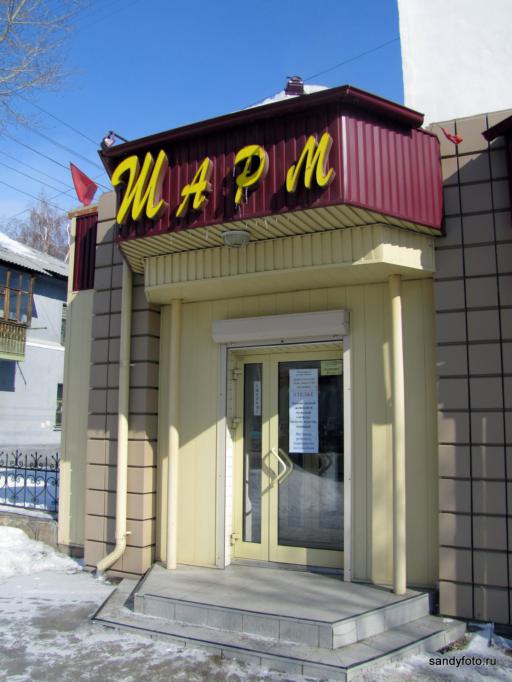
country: RU
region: Chelyabinsk
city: Troitsk
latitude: 54.0880
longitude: 61.5559
